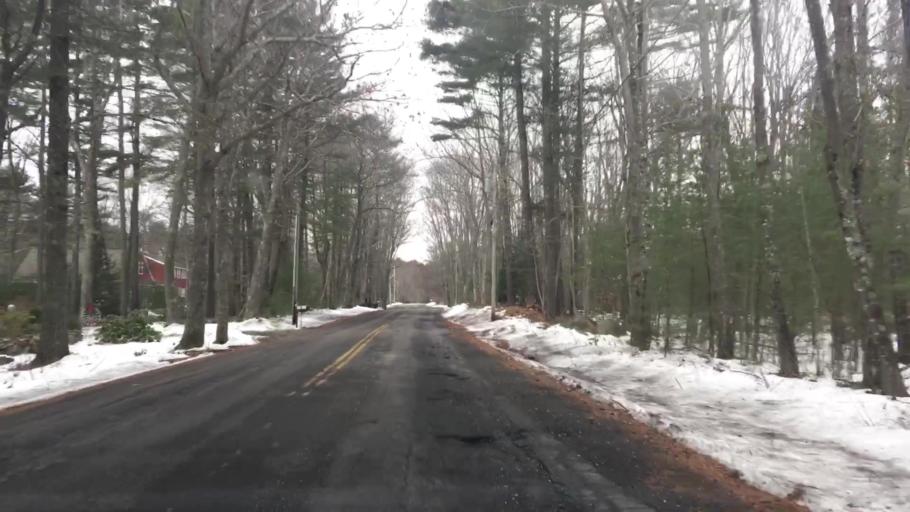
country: US
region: Maine
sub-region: York County
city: Wells Beach Station
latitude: 43.3421
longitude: -70.6124
